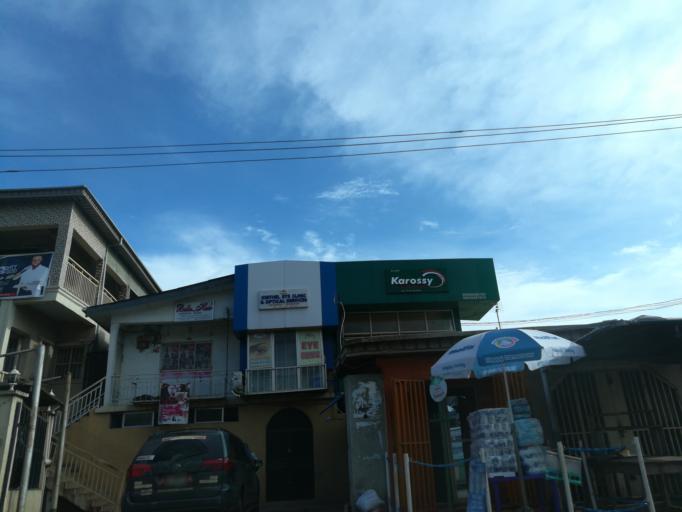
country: NG
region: Lagos
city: Agege
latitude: 6.6008
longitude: 3.3080
